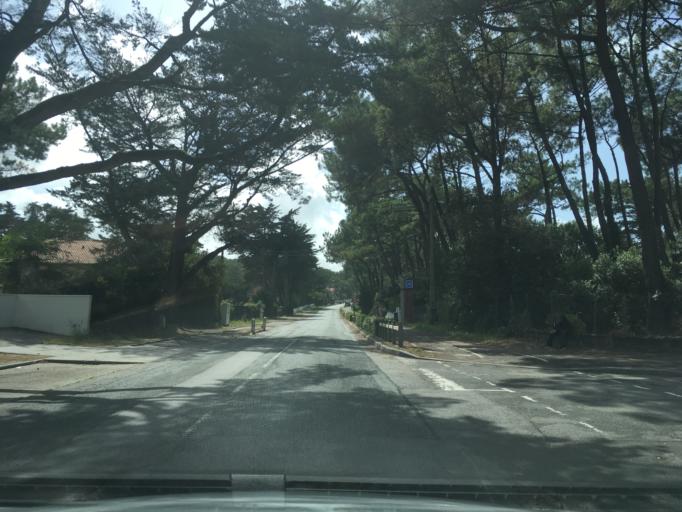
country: FR
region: Aquitaine
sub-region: Departement des Pyrenees-Atlantiques
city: Anglet
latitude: 43.5118
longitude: -1.5272
